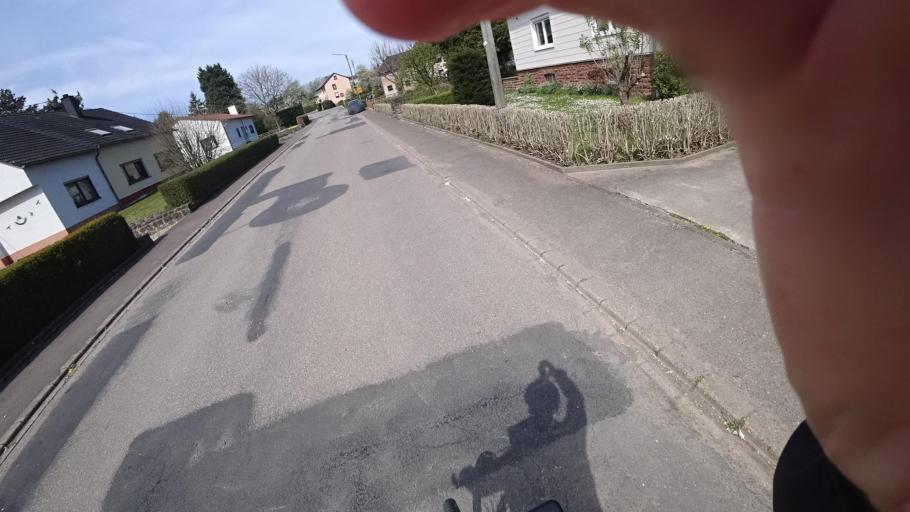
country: DE
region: Rheinland-Pfalz
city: Newel
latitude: 49.8155
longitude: 6.5772
